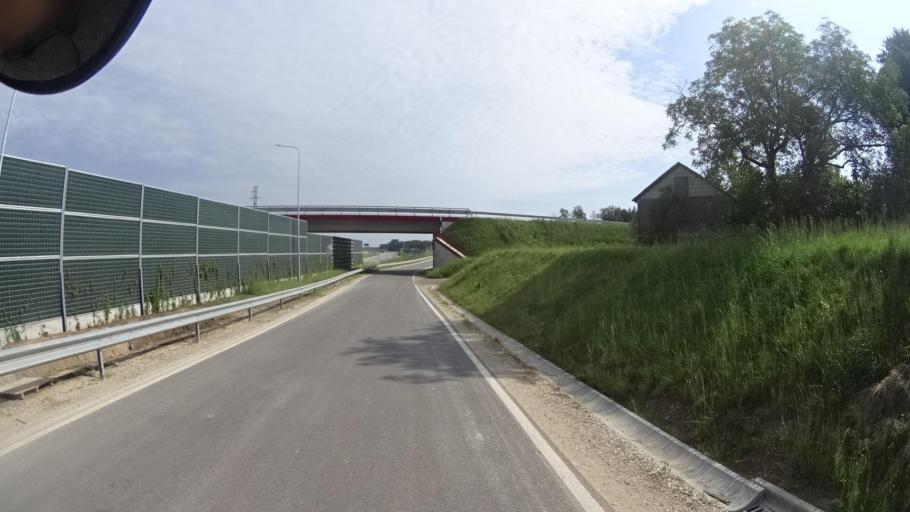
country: PL
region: Masovian Voivodeship
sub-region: Powiat piaseczynski
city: Tarczyn
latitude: 51.9562
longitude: 20.8509
